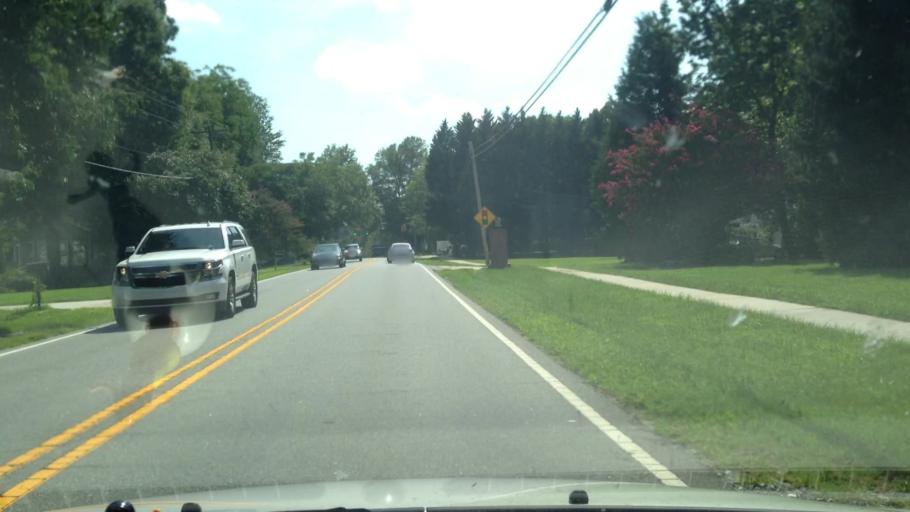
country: US
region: North Carolina
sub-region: Guilford County
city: Oak Ridge
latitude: 36.1713
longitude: -79.9926
